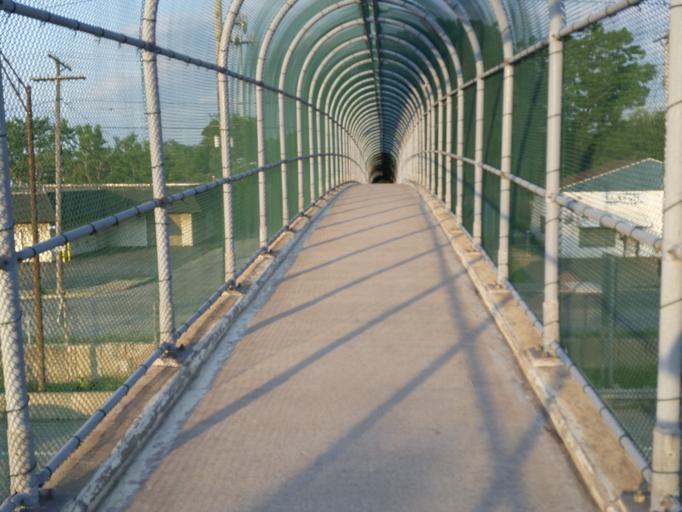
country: US
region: Ohio
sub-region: Cuyahoga County
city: Newburgh Heights
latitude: 41.4599
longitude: -81.6571
